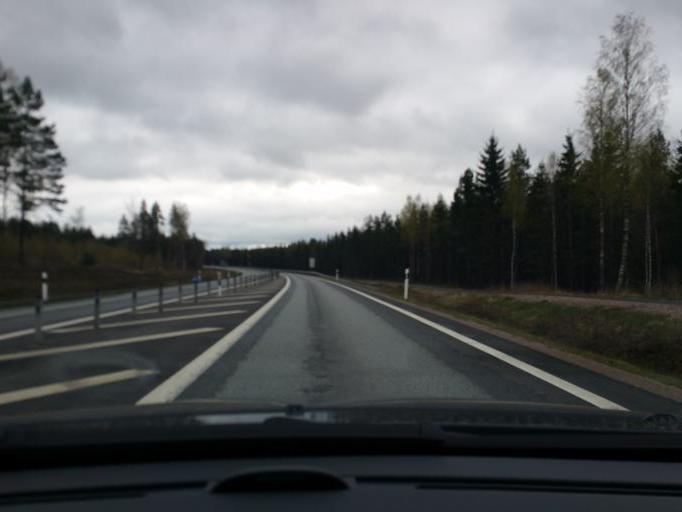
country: SE
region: Kronoberg
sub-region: Vaxjo Kommun
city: Gemla
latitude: 56.9208
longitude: 14.7169
